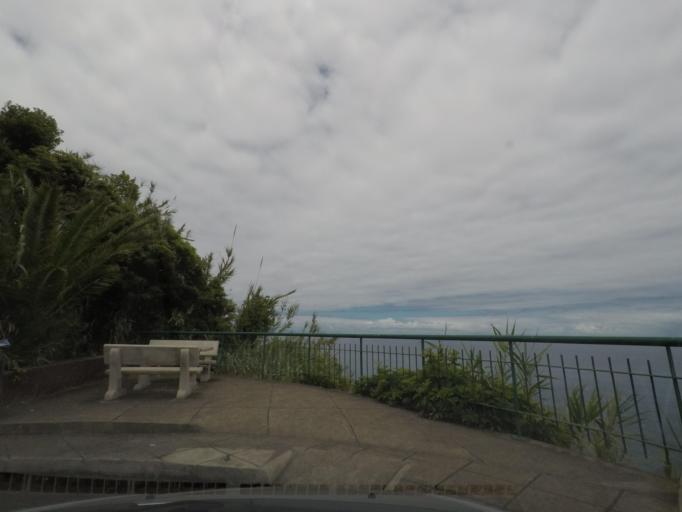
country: PT
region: Madeira
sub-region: Santana
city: Santana
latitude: 32.8290
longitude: -16.9525
